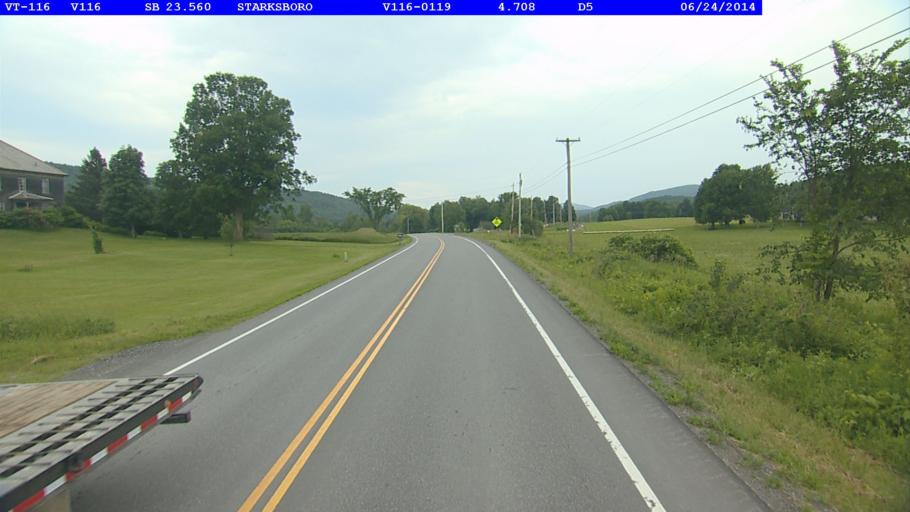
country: US
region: Vermont
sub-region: Chittenden County
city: Hinesburg
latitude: 44.2520
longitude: -73.0629
